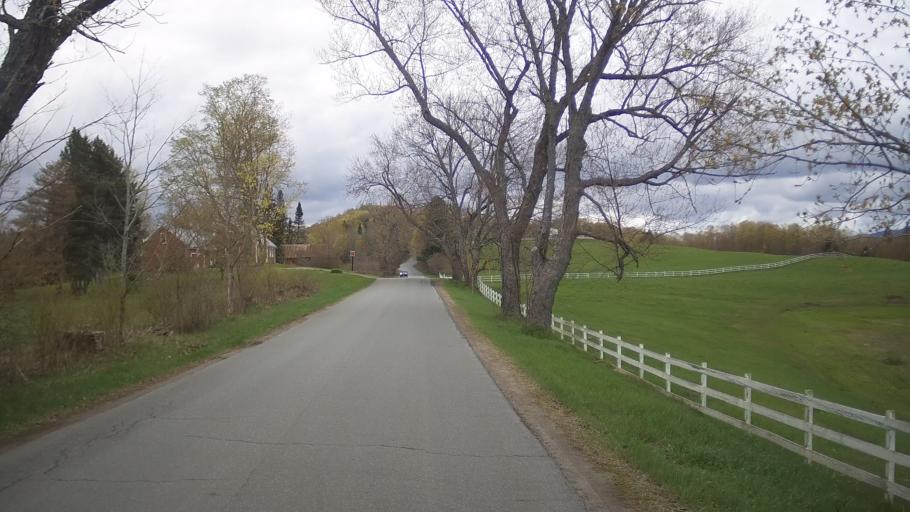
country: US
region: Vermont
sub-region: Caledonia County
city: Lyndonville
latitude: 44.5915
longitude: -71.9591
